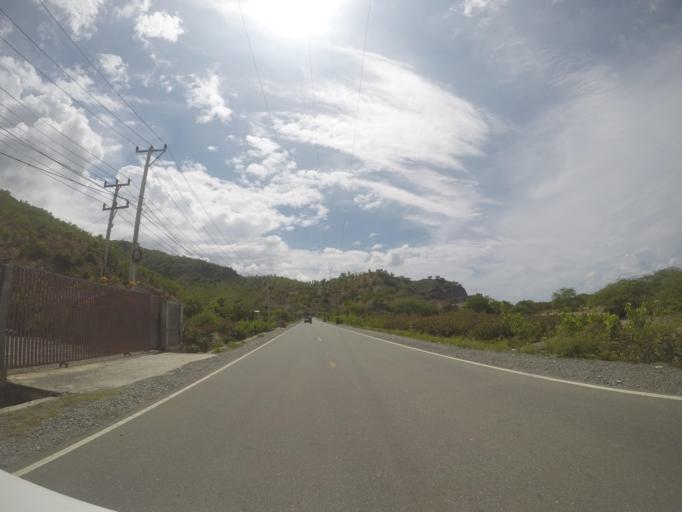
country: TL
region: Liquica
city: Liquica
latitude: -8.5733
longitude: 125.3770
